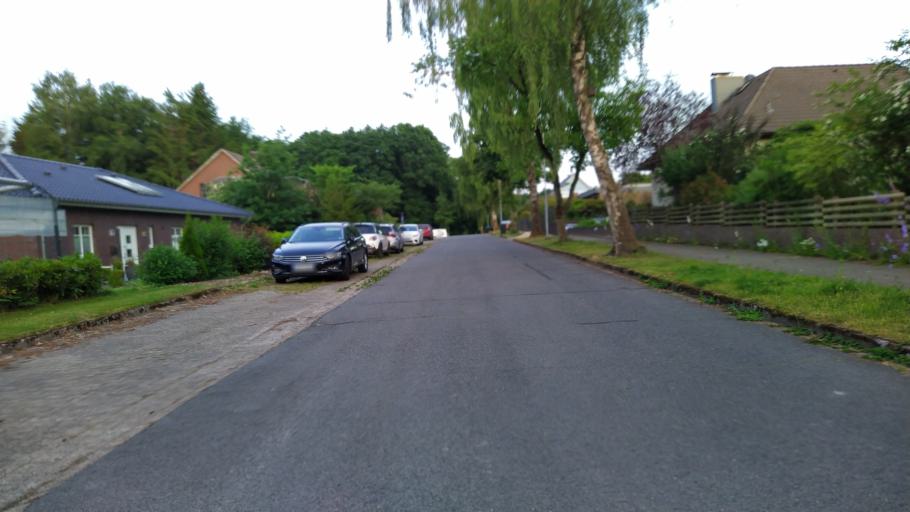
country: DE
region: Lower Saxony
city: Harsefeld
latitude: 53.4813
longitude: 9.5161
